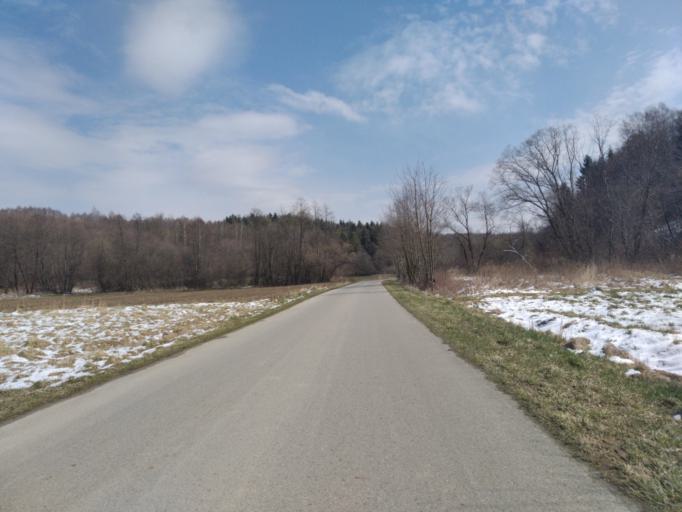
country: PL
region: Subcarpathian Voivodeship
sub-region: Powiat ropczycko-sedziszowski
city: Niedzwiada
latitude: 50.0067
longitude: 21.5736
